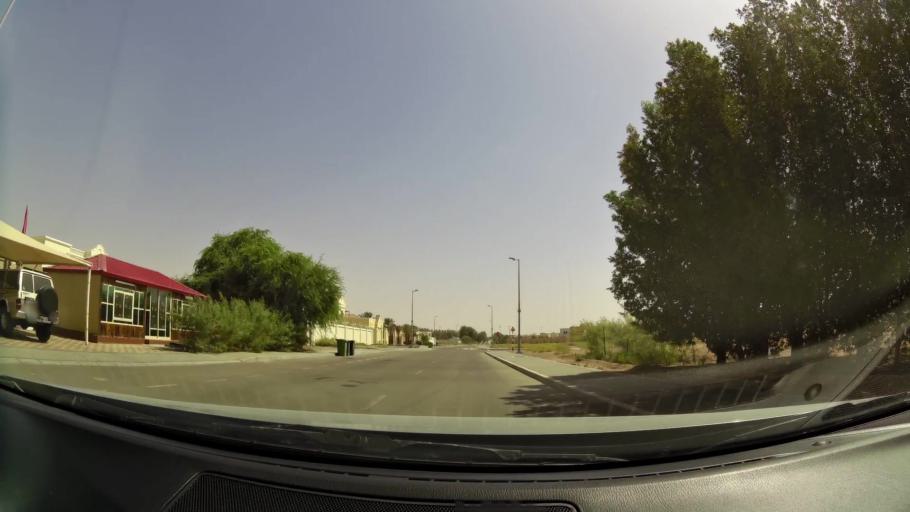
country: OM
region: Al Buraimi
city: Al Buraymi
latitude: 24.3103
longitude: 55.7492
